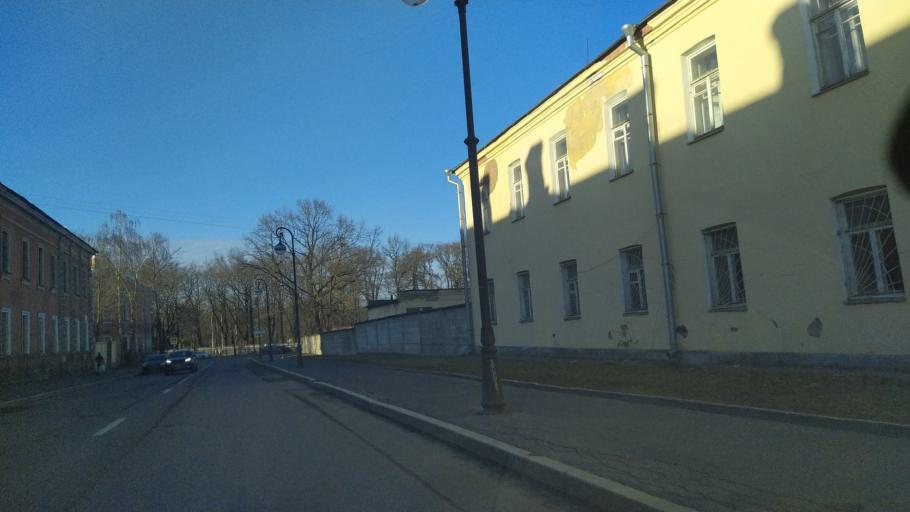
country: RU
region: St.-Petersburg
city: Pushkin
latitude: 59.7072
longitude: 30.3905
